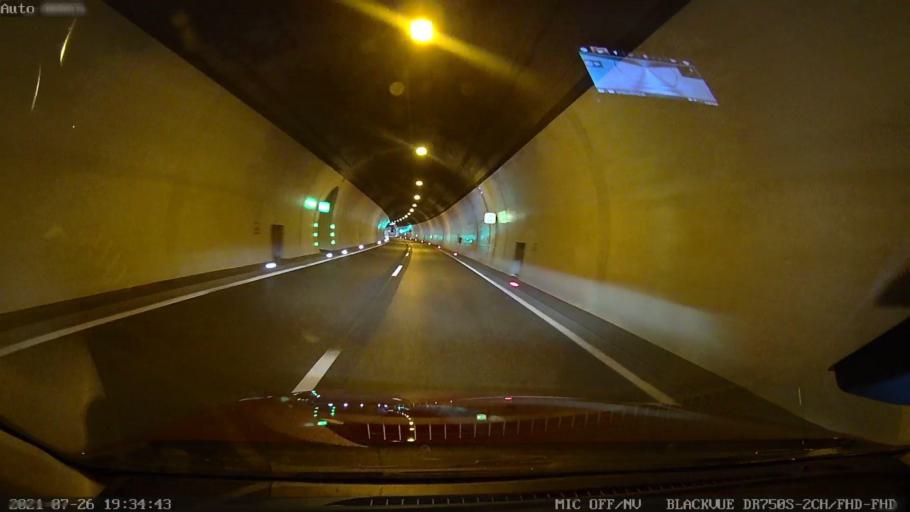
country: AT
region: Upper Austria
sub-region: Politischer Bezirk Kirchdorf an der Krems
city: Rossleithen
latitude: 47.7553
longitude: 14.2266
